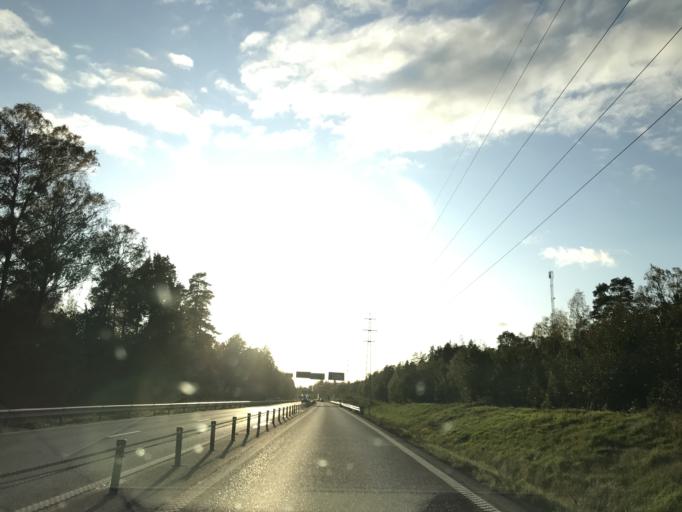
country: SE
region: Kronoberg
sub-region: Vaxjo Kommun
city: Vaexjoe
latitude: 56.9018
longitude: 14.8000
